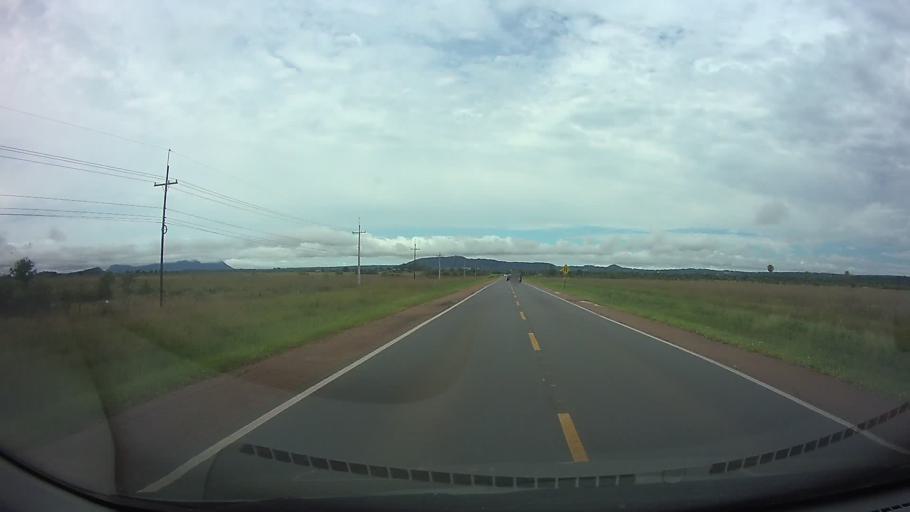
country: PY
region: Paraguari
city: Carapegua
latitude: -25.7373
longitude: -57.2102
